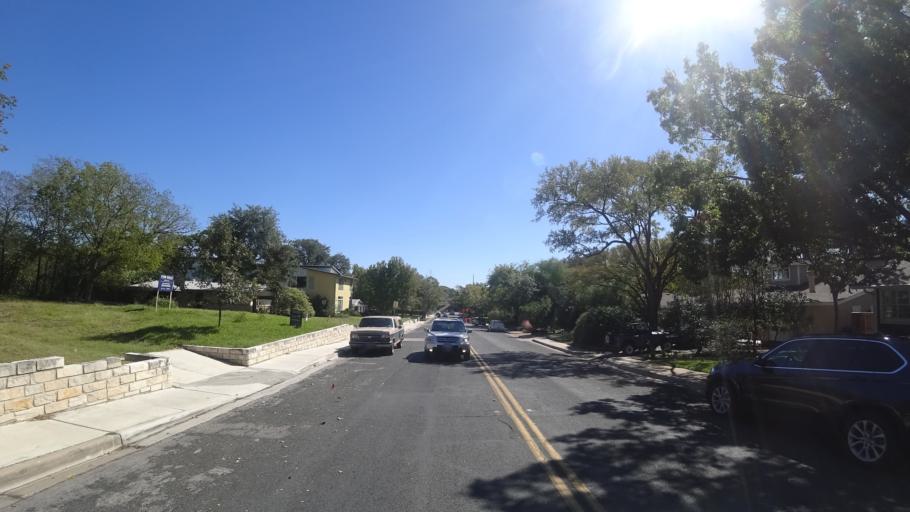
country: US
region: Texas
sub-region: Travis County
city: Austin
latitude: 30.3013
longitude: -97.7607
